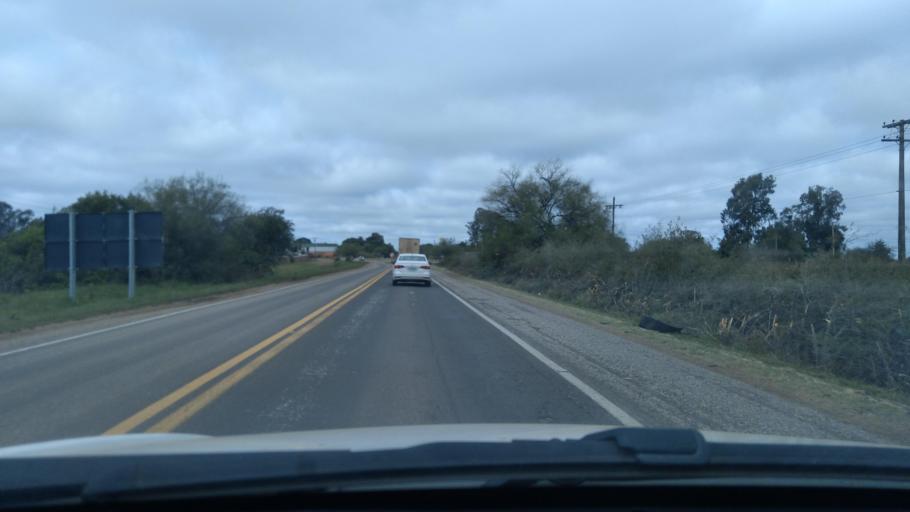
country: BR
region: Rio Grande do Sul
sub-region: Dom Pedrito
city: Dom Pedrito
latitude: -30.9824
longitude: -54.6404
